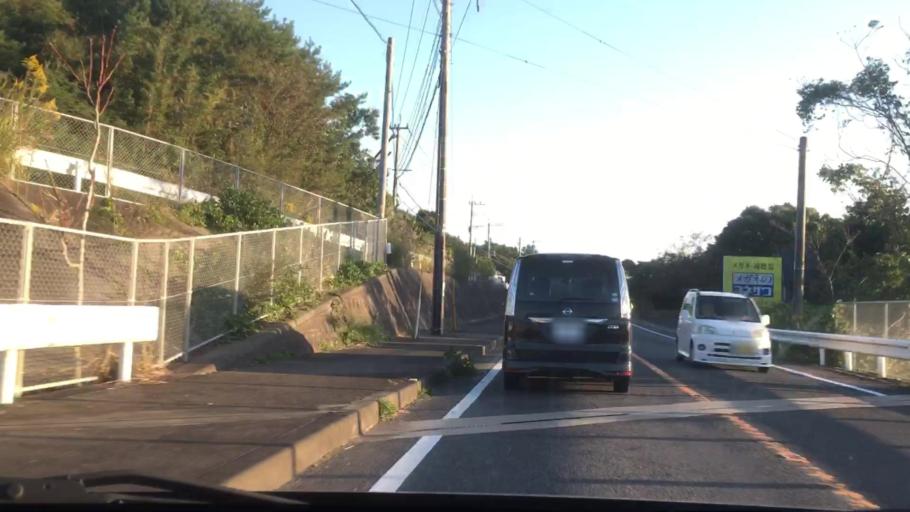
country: JP
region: Nagasaki
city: Sasebo
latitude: 33.0677
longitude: 129.7640
